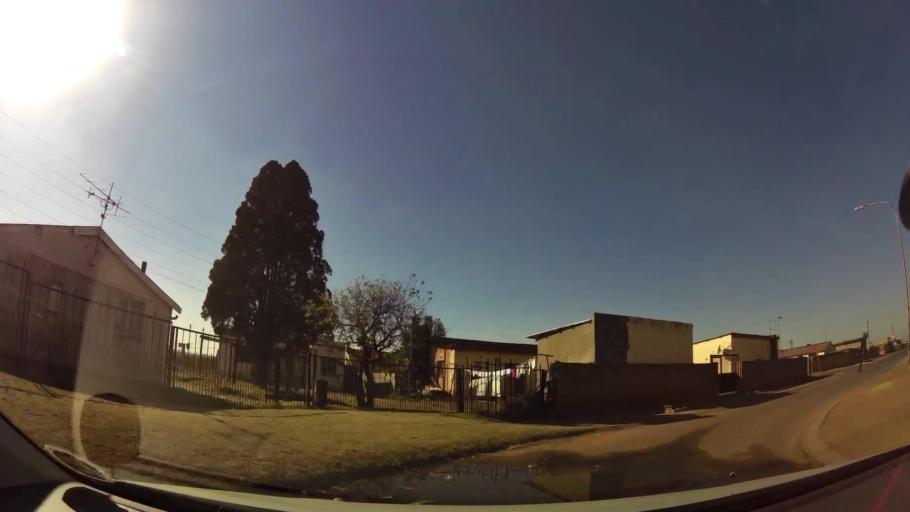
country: ZA
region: Gauteng
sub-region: City of Johannesburg Metropolitan Municipality
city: Roodepoort
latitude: -26.2086
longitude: 27.8985
